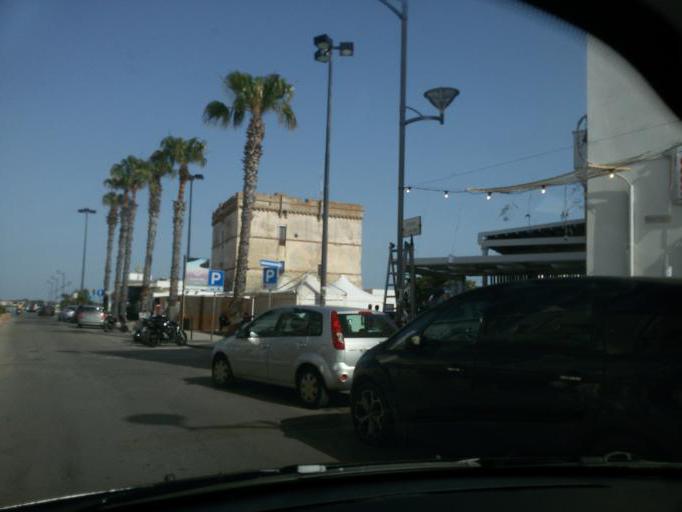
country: IT
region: Apulia
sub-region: Provincia di Lecce
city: Porto Cesareo
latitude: 40.2575
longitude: 17.8911
